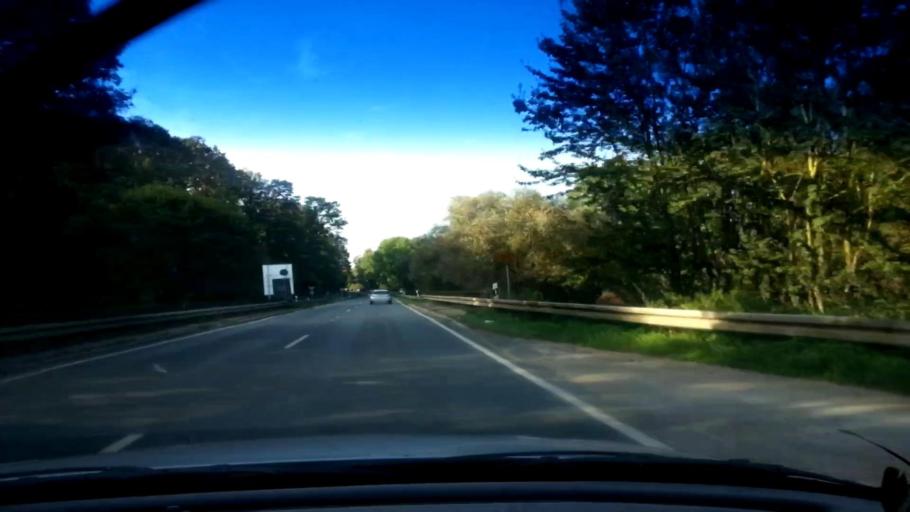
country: DE
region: Bavaria
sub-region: Upper Franconia
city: Baunach
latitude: 49.9803
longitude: 10.8581
